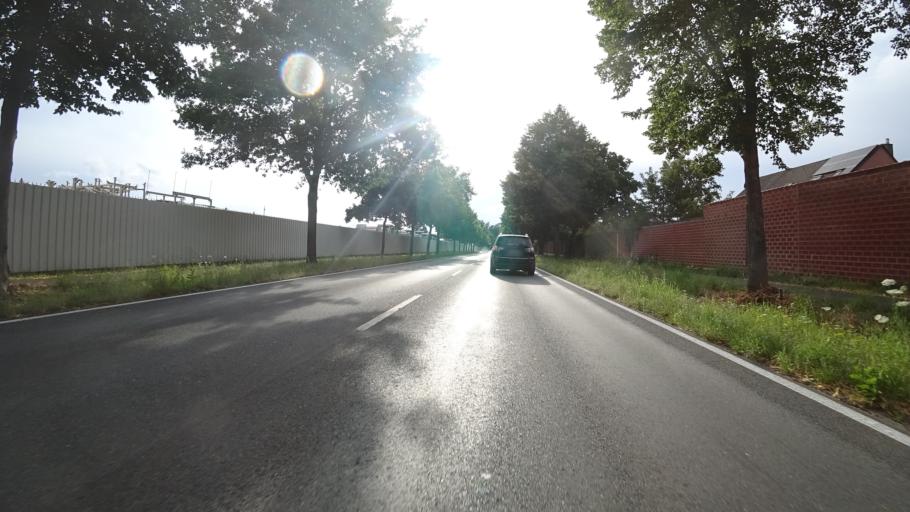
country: DE
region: North Rhine-Westphalia
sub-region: Regierungsbezirk Detmold
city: Harsewinkel
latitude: 51.9638
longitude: 8.2064
